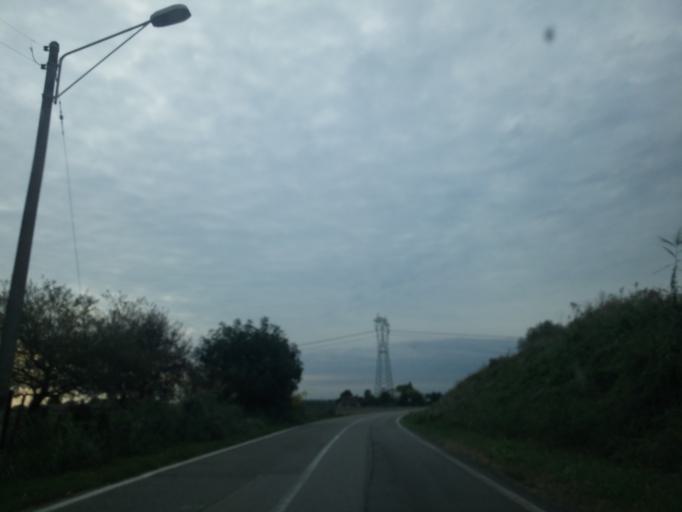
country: IT
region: Emilia-Romagna
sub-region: Provincia di Bologna
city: Longara
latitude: 44.5898
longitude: 11.3190
